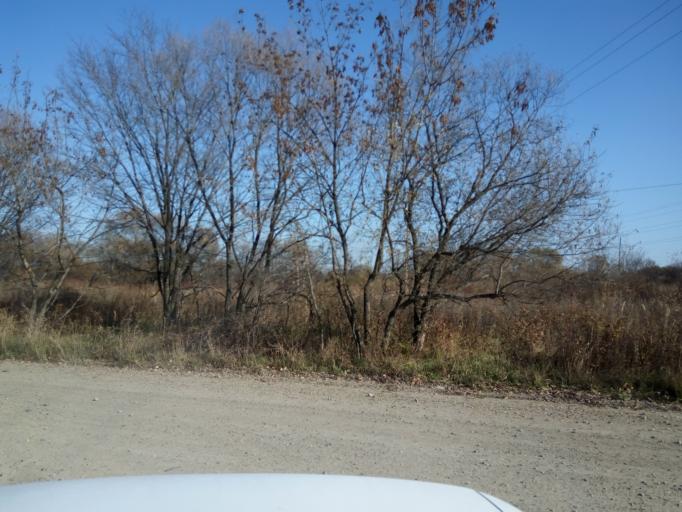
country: RU
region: Primorskiy
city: Dal'nerechensk
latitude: 45.9153
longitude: 133.7147
